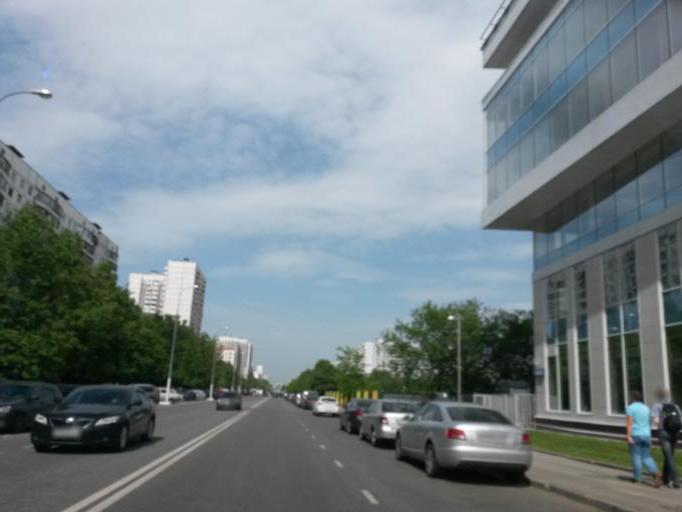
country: RU
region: Moscow
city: Chertanovo Yuzhnoye
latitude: 55.6008
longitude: 37.5985
